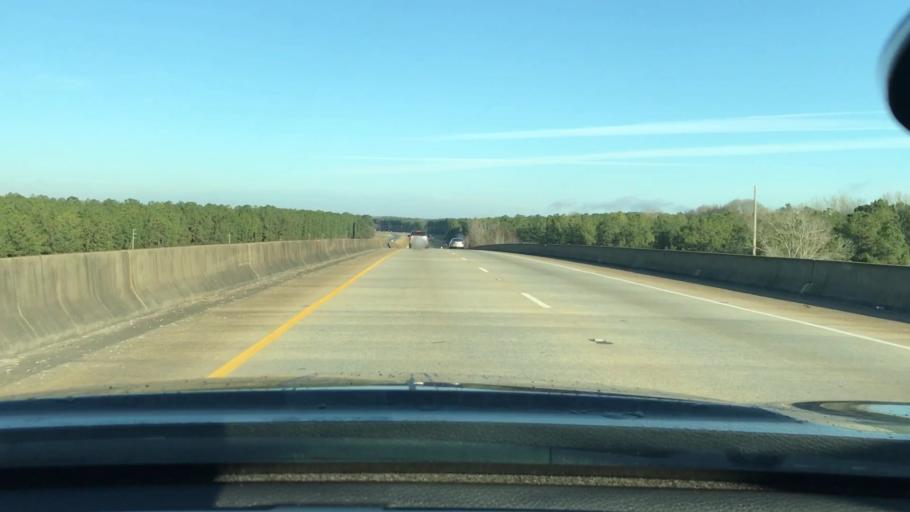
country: US
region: Alabama
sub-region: Talladega County
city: Childersburg
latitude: 33.2911
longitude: -86.3651
